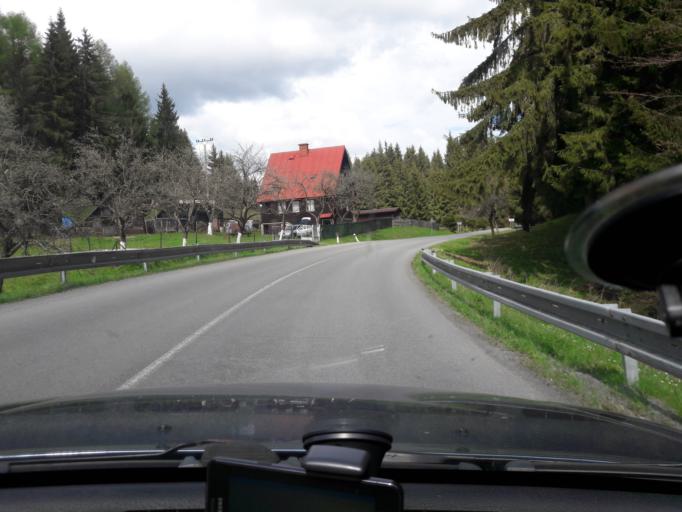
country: SK
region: Banskobystricky
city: Hrinova
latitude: 48.6433
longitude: 19.6100
